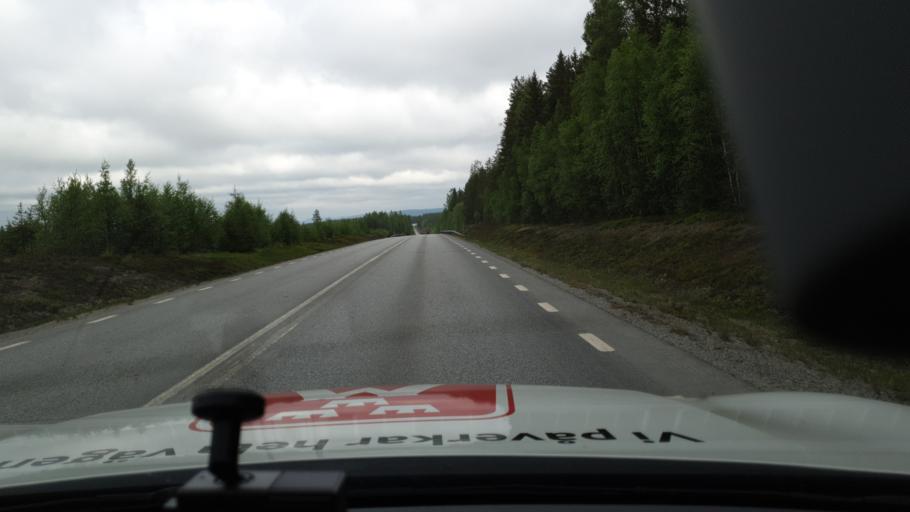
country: SE
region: Vaesterbotten
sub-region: Vannas Kommun
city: Vannasby
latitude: 64.0511
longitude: 19.9978
